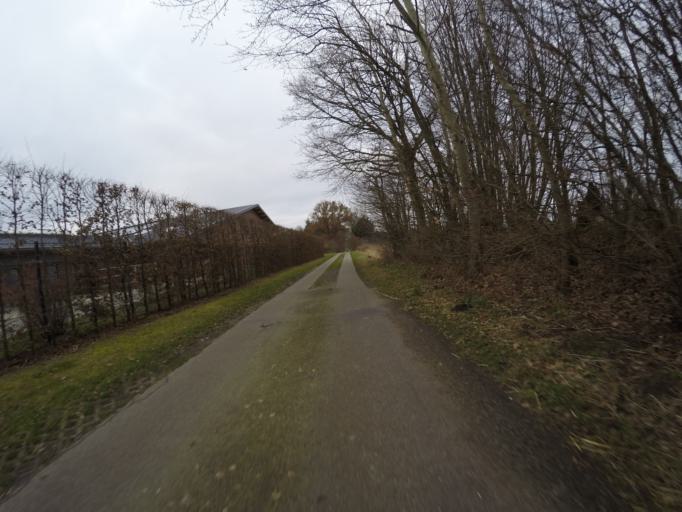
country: DE
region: Schleswig-Holstein
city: Hemdingen
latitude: 53.7725
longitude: 9.8425
